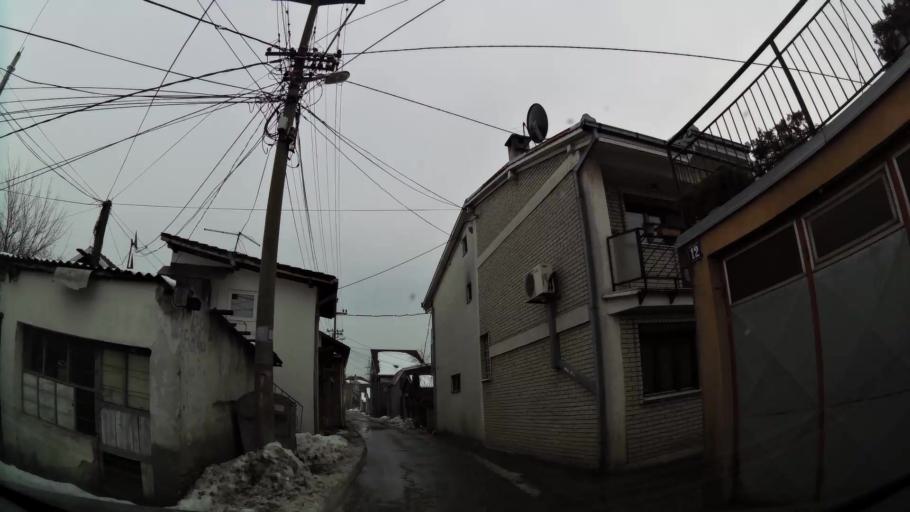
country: RS
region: Central Serbia
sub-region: Belgrade
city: Zemun
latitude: 44.8333
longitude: 20.3766
